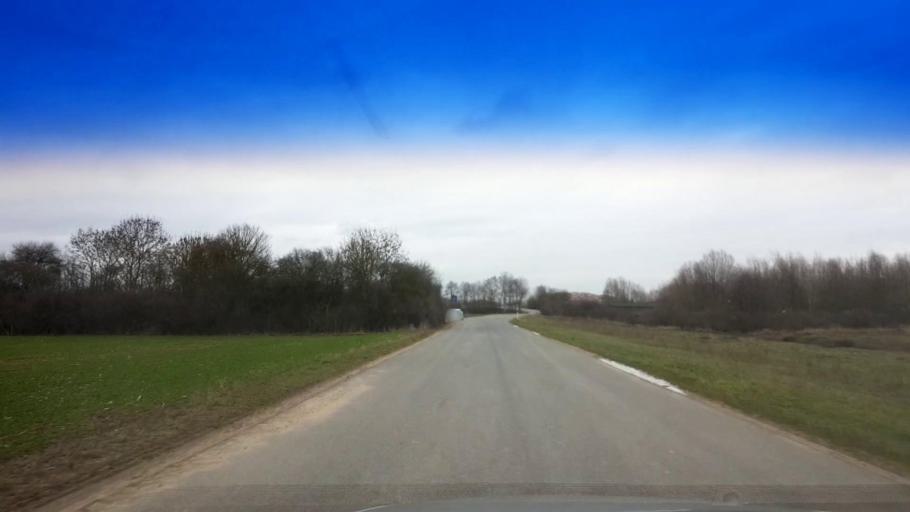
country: DE
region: Bavaria
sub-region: Upper Franconia
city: Viereth-Trunstadt
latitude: 49.9293
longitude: 10.7716
